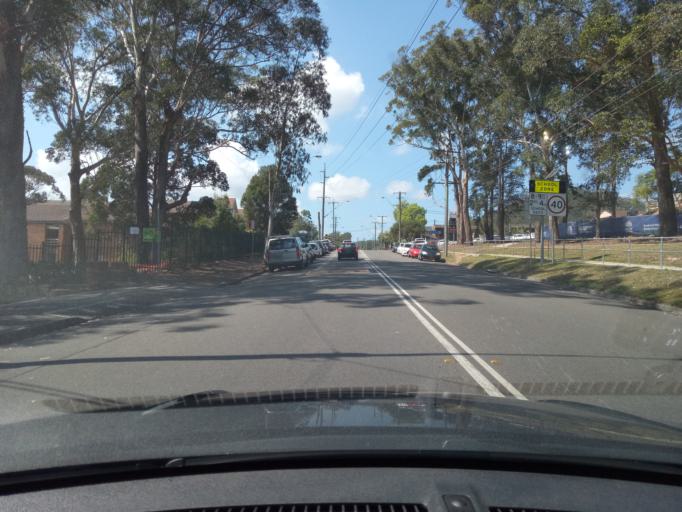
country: AU
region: New South Wales
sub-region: Gosford Shire
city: Gosford
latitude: -33.4185
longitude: 151.3402
